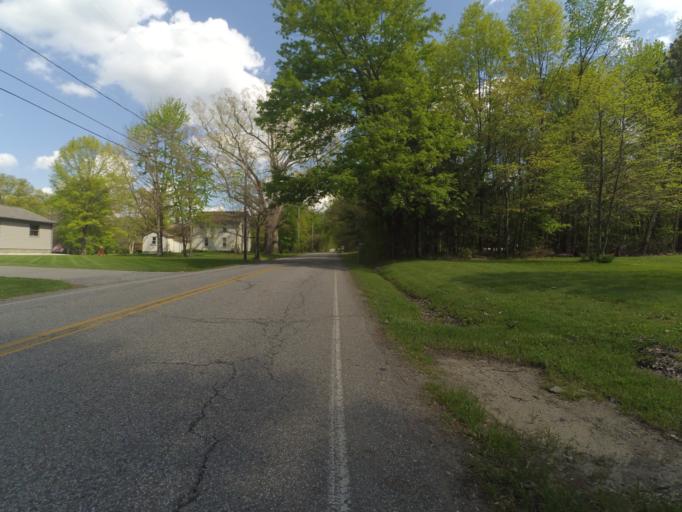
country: US
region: Ohio
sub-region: Trumbull County
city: Mineral Ridge
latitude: 41.1330
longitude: -80.7763
